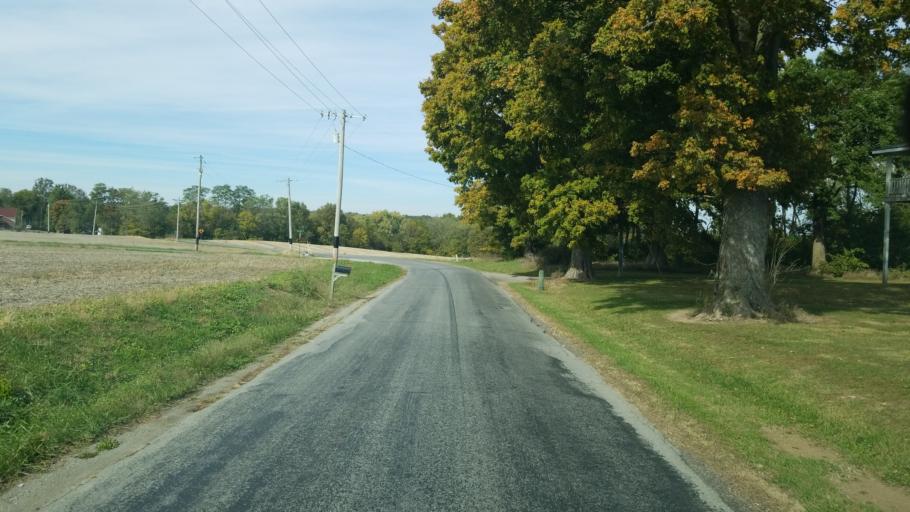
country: US
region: Ohio
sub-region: Highland County
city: Leesburg
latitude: 39.3246
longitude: -83.4735
